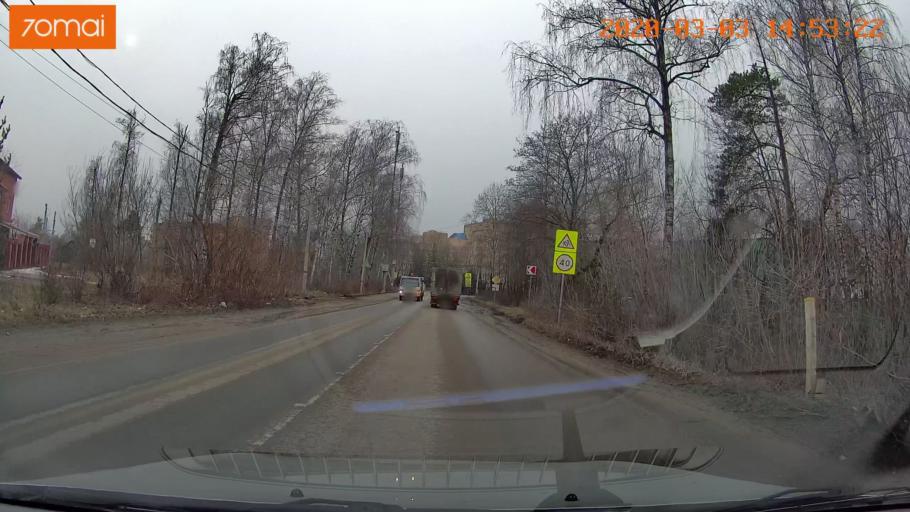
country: RU
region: Moskovskaya
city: Korenevo
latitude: 55.6742
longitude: 38.0096
